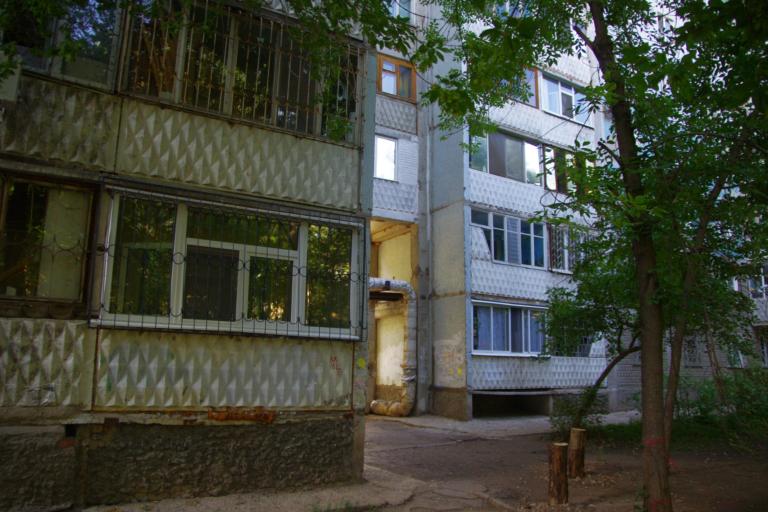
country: RU
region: Samara
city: Samara
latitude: 53.1956
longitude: 50.1429
